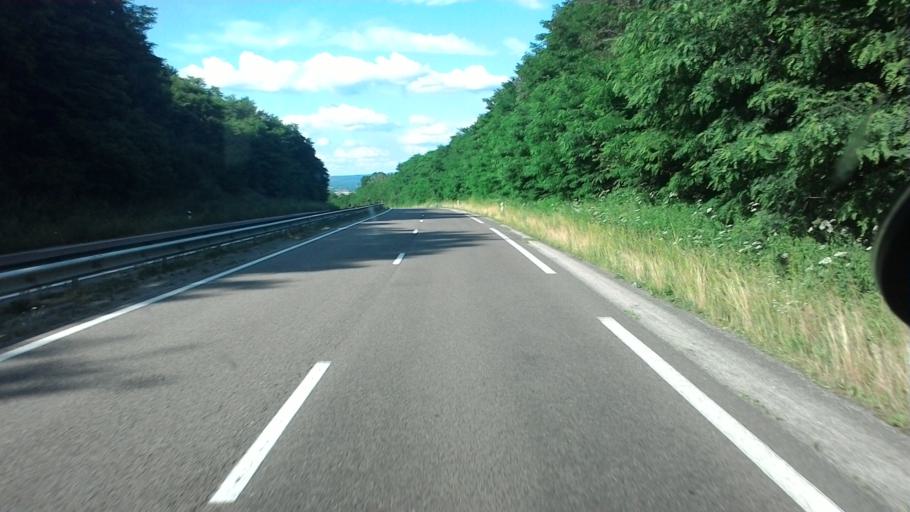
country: FR
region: Franche-Comte
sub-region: Departement de la Haute-Saone
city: Luxeuil-les-Bains
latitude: 47.7469
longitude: 6.3279
